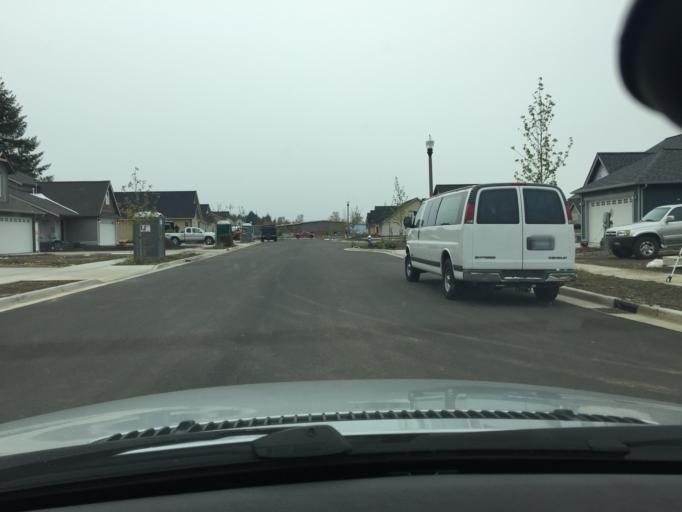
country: US
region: Washington
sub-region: Whatcom County
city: Lynden
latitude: 48.9591
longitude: -122.4103
